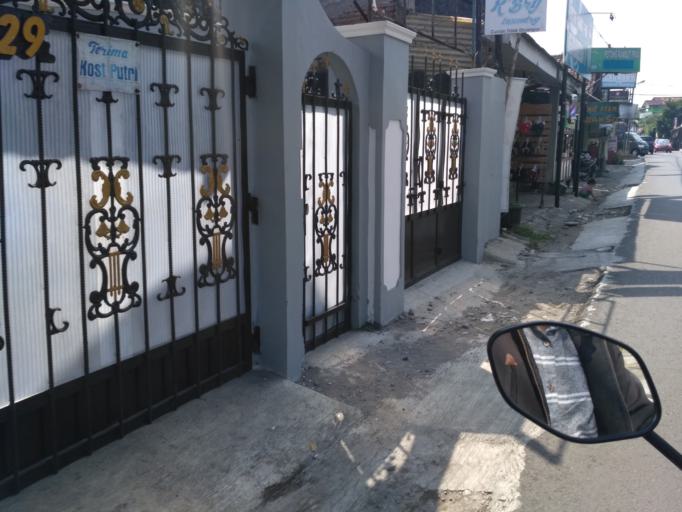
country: ID
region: Daerah Istimewa Yogyakarta
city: Depok
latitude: -7.7794
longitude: 110.4085
